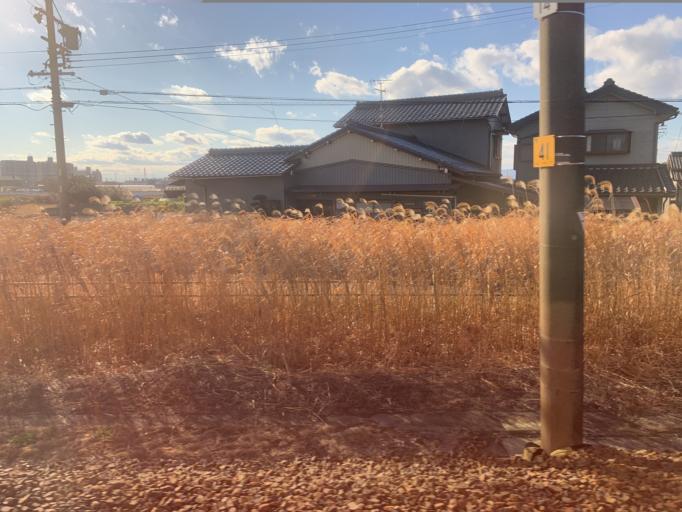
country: JP
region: Aichi
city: Inazawa
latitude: 35.2629
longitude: 136.8161
